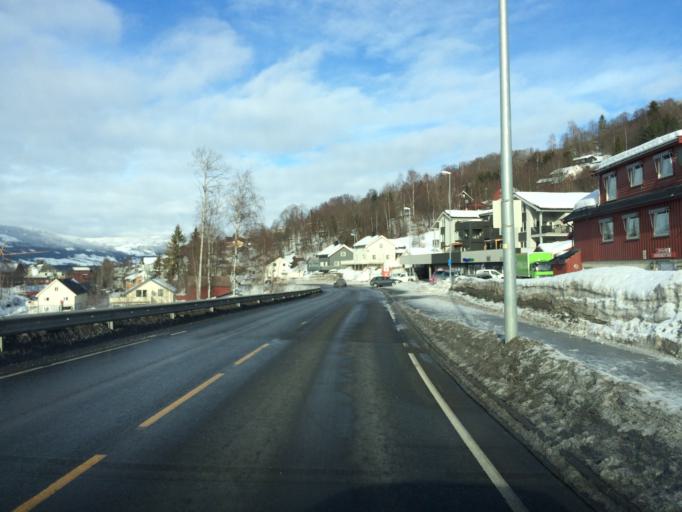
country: NO
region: Oppland
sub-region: Gausdal
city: Segalstad bru
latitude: 61.2259
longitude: 10.2277
